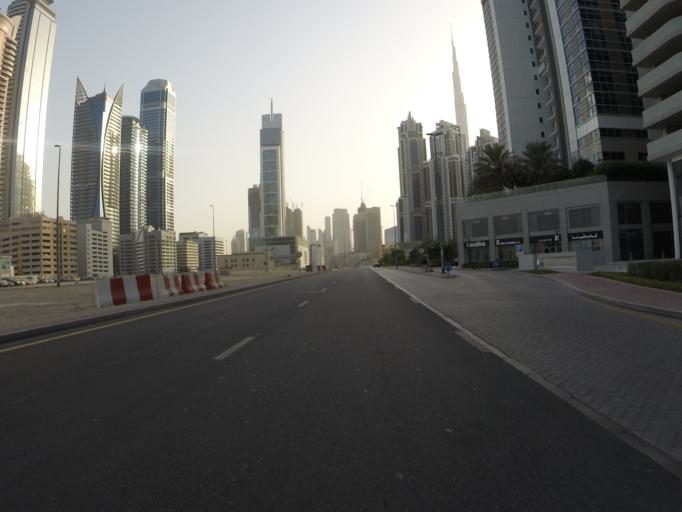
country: AE
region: Dubai
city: Dubai
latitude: 25.1892
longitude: 55.2624
